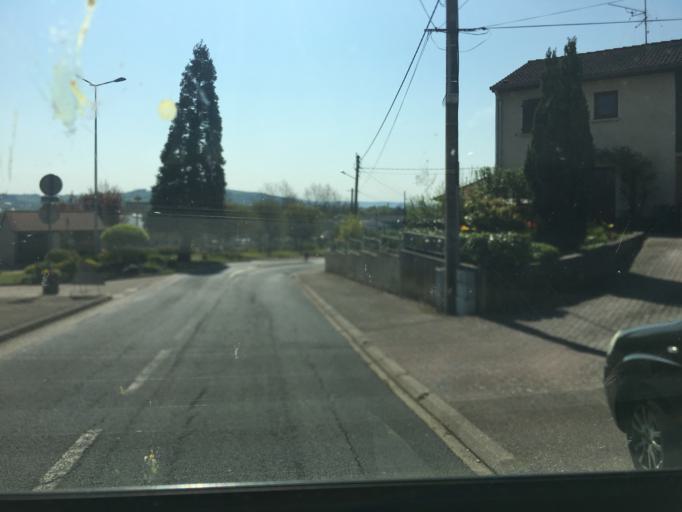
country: FR
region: Lorraine
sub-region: Departement de Meurthe-et-Moselle
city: Norroy-les-Pont-a-Mousson
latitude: 48.9325
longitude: 6.0366
